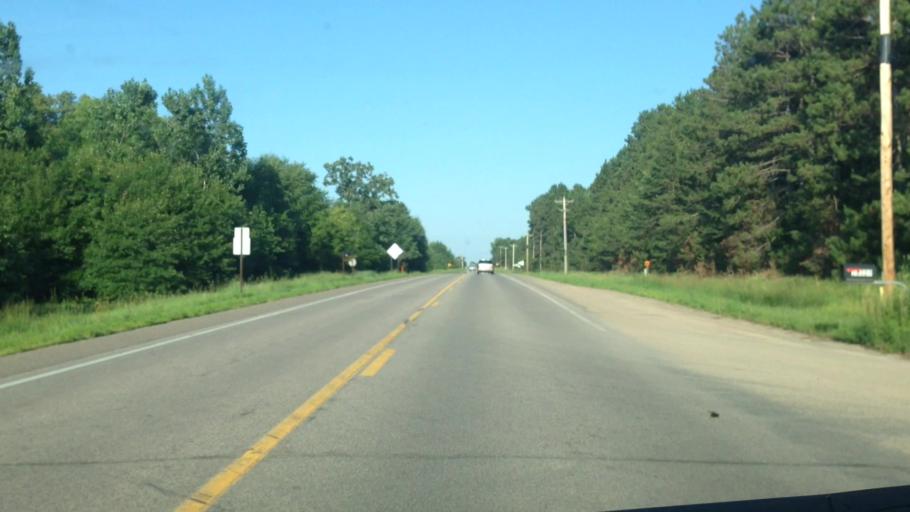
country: US
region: Minnesota
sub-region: Sherburne County
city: Big Lake
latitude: 45.4477
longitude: -93.7343
